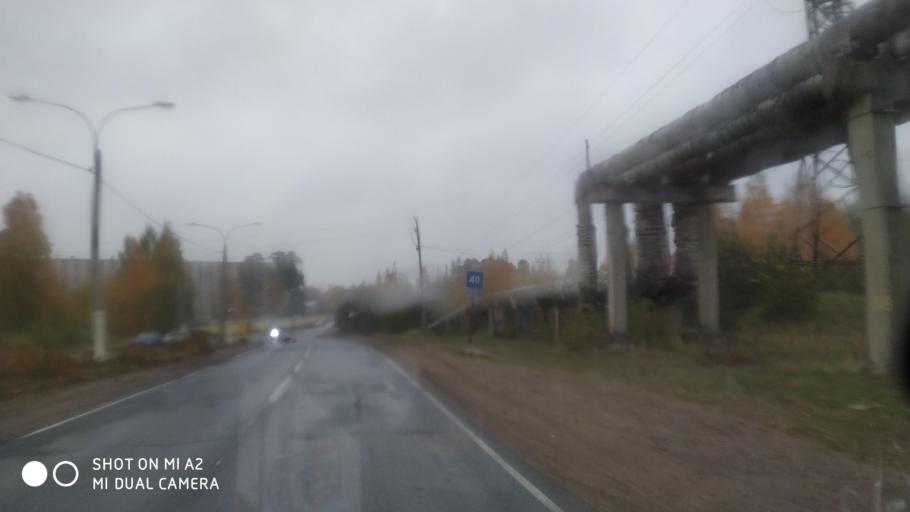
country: RU
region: Leningrad
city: Sosnovyy Bor
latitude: 59.8902
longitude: 29.1037
